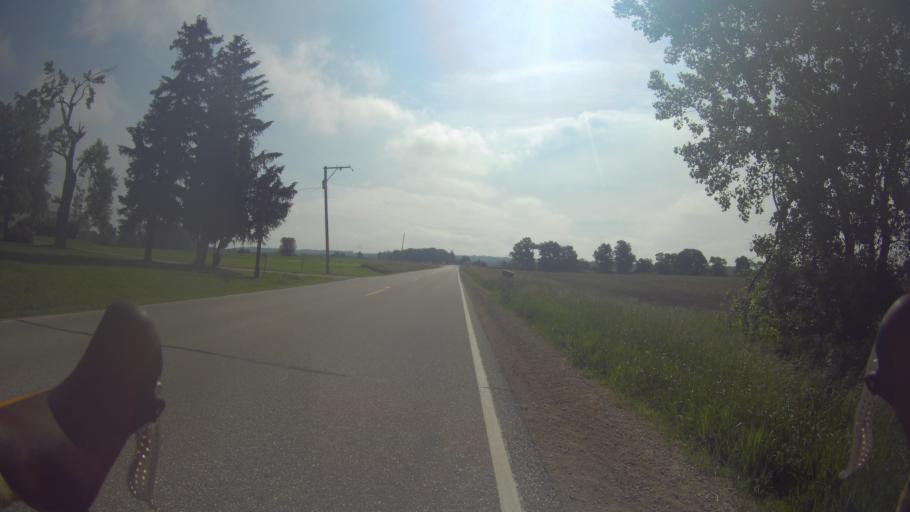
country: US
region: Wisconsin
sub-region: Dane County
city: McFarland
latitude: 43.0149
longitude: -89.2502
